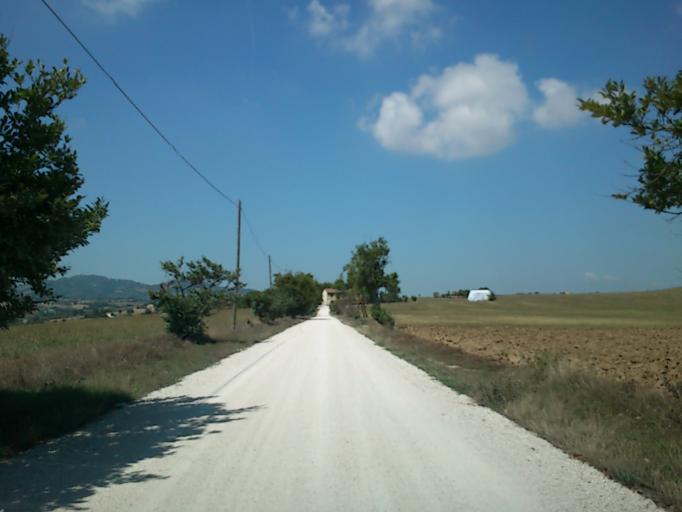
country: IT
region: The Marches
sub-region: Provincia di Pesaro e Urbino
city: Lucrezia
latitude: 43.7770
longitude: 12.9309
